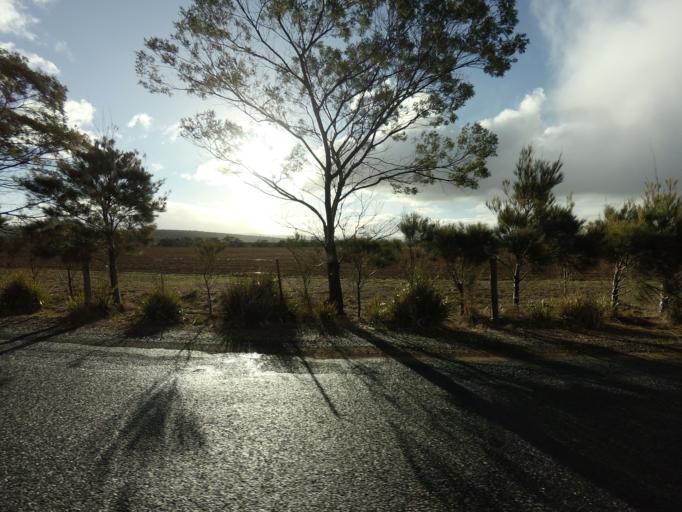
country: AU
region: Tasmania
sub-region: Break O'Day
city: St Helens
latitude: -42.0980
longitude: 148.0666
